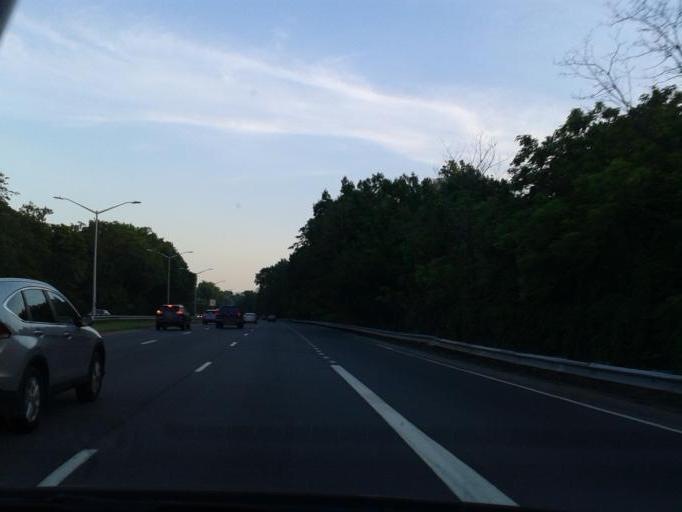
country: US
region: New York
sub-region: Bronx
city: The Bronx
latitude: 40.8763
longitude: -73.8709
